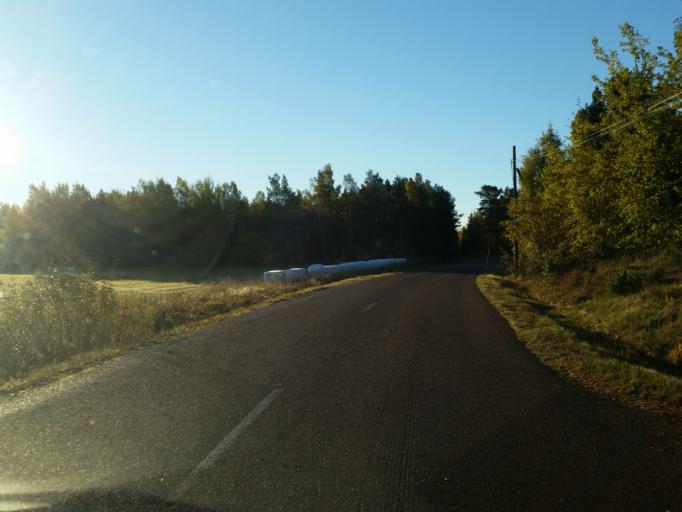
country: AX
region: Alands skaergard
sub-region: Vardoe
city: Vardoe
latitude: 60.2954
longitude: 20.3858
